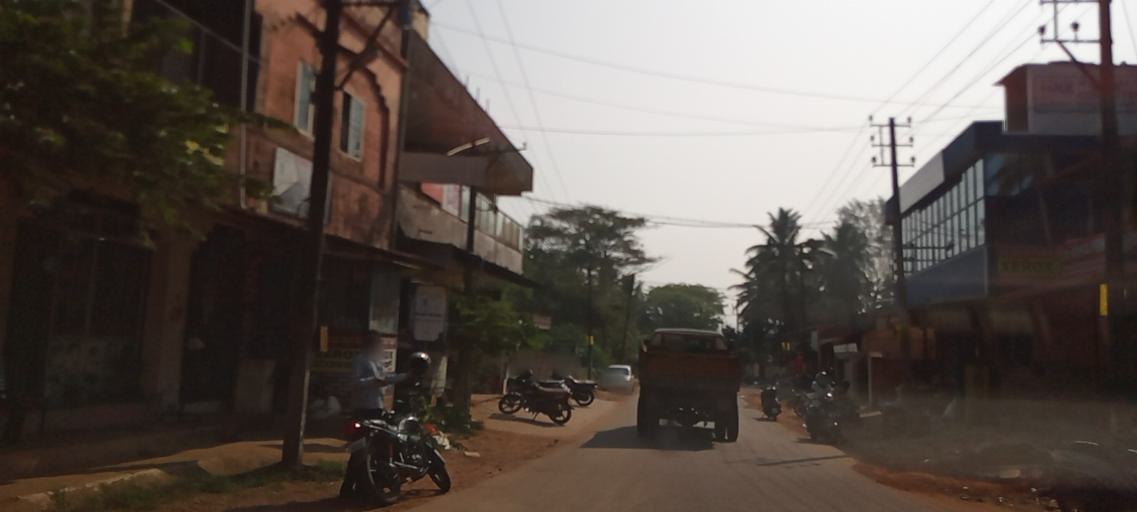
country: IN
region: Karnataka
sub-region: Udupi
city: Coondapoor
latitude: 13.5089
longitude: 74.7078
